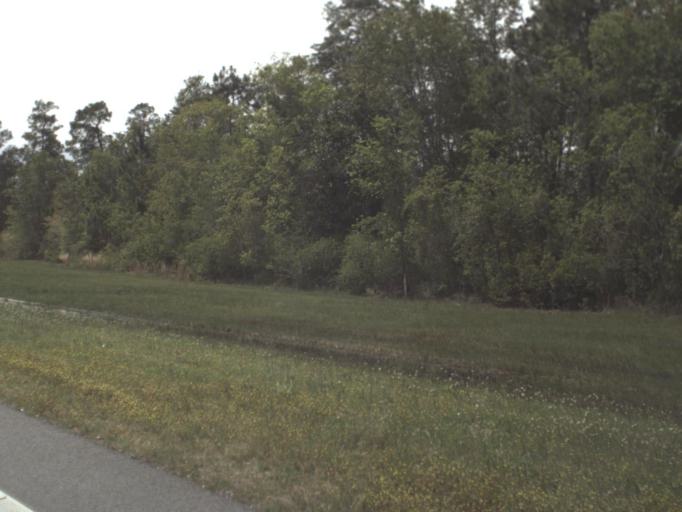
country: US
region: Florida
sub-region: Escambia County
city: Myrtle Grove
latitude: 30.4114
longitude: -87.3385
